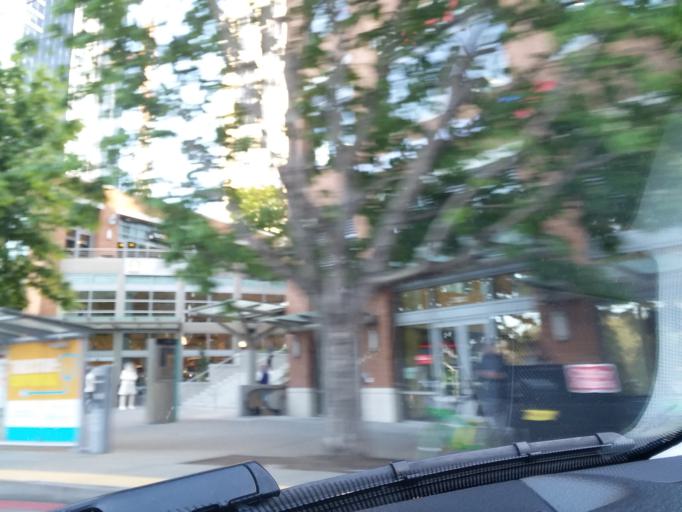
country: US
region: Washington
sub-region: King County
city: Seattle
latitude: 47.6180
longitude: -122.3385
